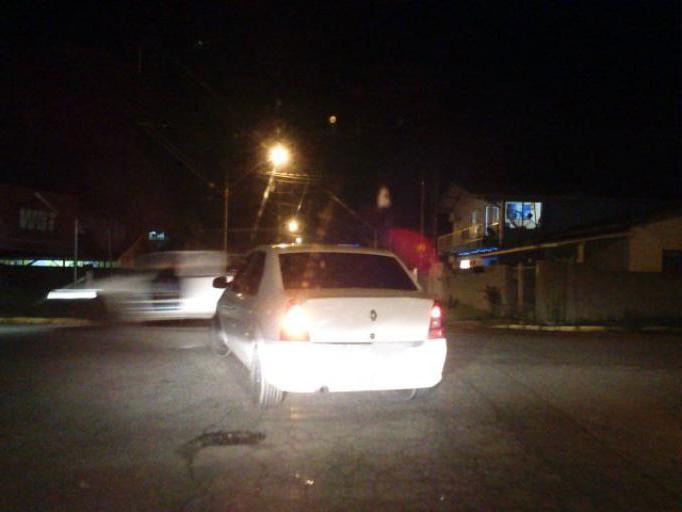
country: BR
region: Santa Catarina
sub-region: Itapema
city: Itapema
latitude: -27.1207
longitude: -48.6124
